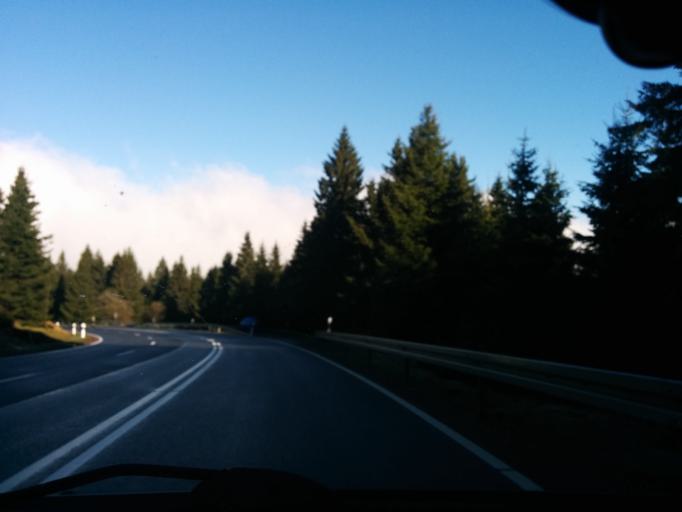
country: DE
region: Lower Saxony
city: Altenau
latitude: 51.7716
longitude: 10.4536
